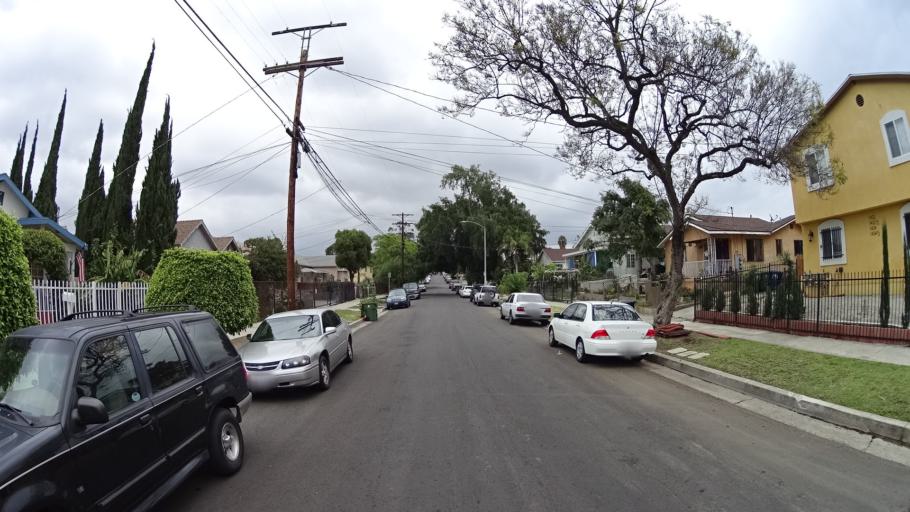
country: US
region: California
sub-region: Los Angeles County
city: Boyle Heights
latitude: 34.0594
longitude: -118.1985
